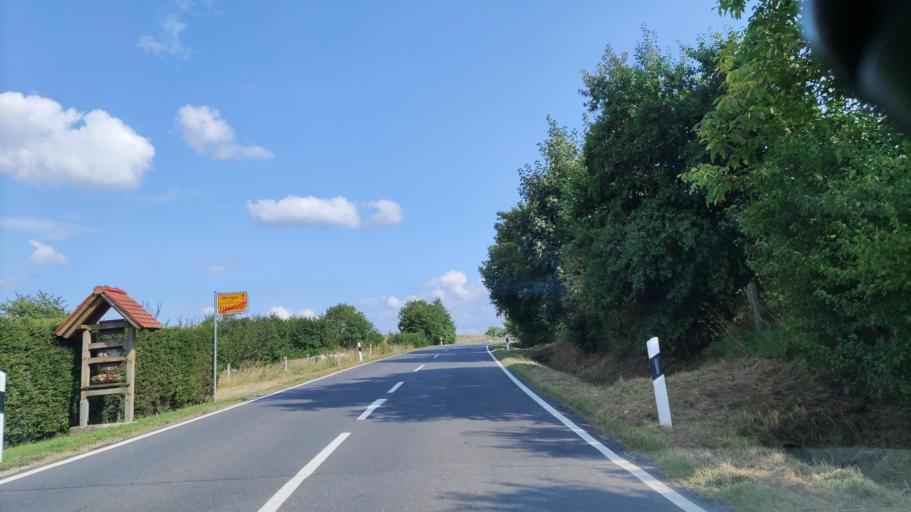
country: DE
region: Lower Saxony
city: Moringen
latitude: 51.7358
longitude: 9.8003
